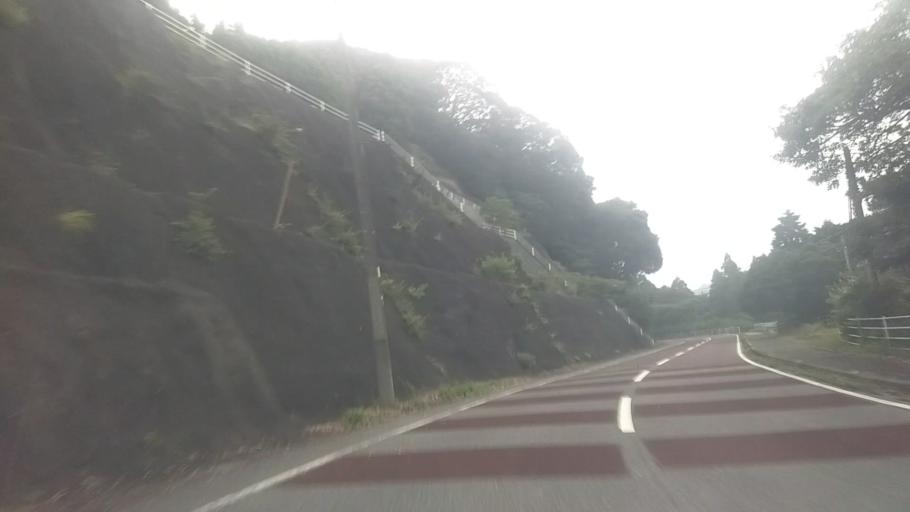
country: JP
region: Chiba
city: Kawaguchi
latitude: 35.1493
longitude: 140.1490
